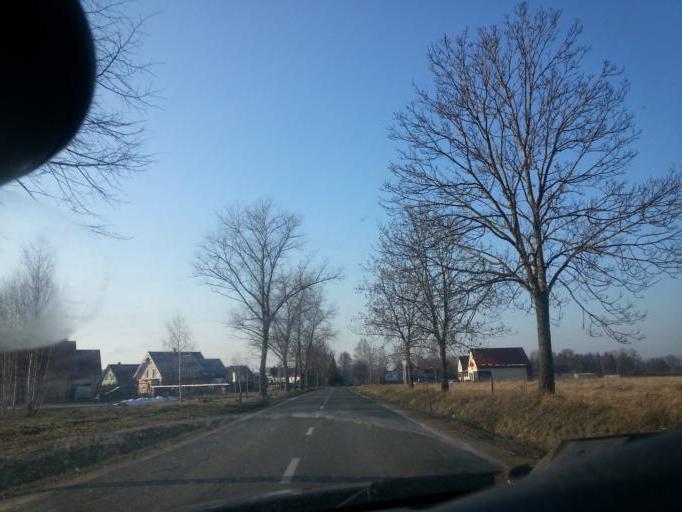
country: PL
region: Lower Silesian Voivodeship
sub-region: Powiat jeleniogorski
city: Myslakowice
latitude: 50.8320
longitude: 15.7913
